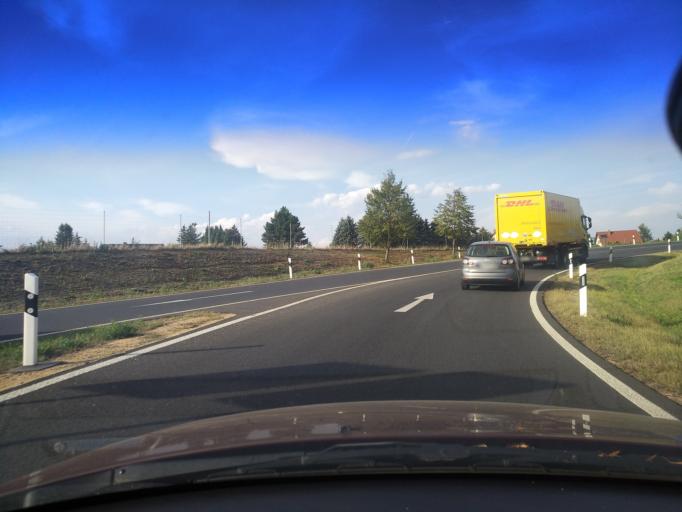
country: DE
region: Saxony
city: Bautzen
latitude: 51.1963
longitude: 14.4637
